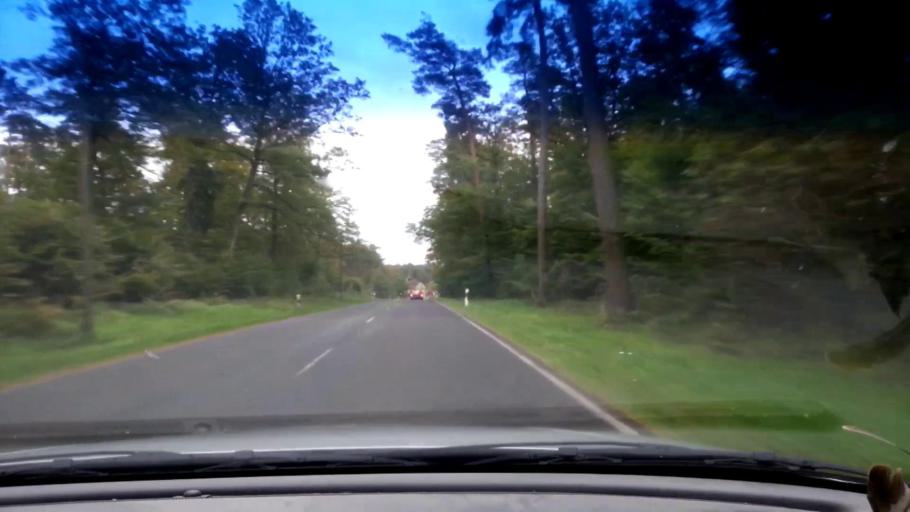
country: DE
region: Bavaria
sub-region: Upper Franconia
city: Lauter
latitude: 49.9613
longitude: 10.8087
